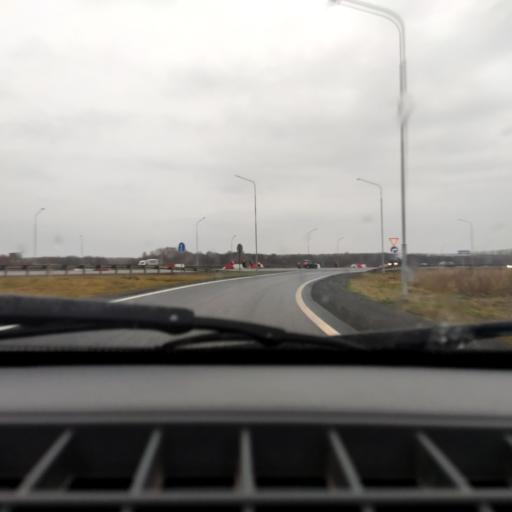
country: RU
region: Bashkortostan
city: Avdon
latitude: 54.6646
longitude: 55.7378
